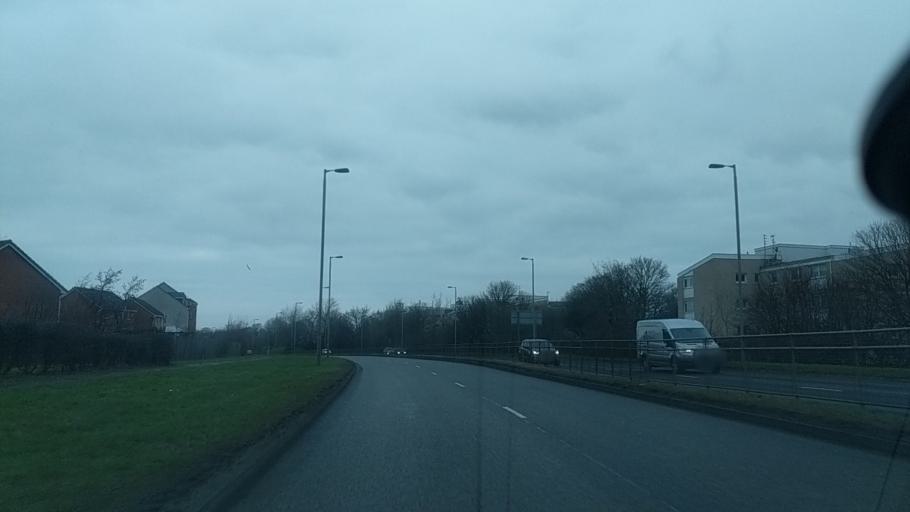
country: GB
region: Scotland
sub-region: South Lanarkshire
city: East Kilbride
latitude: 55.7595
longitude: -4.1650
